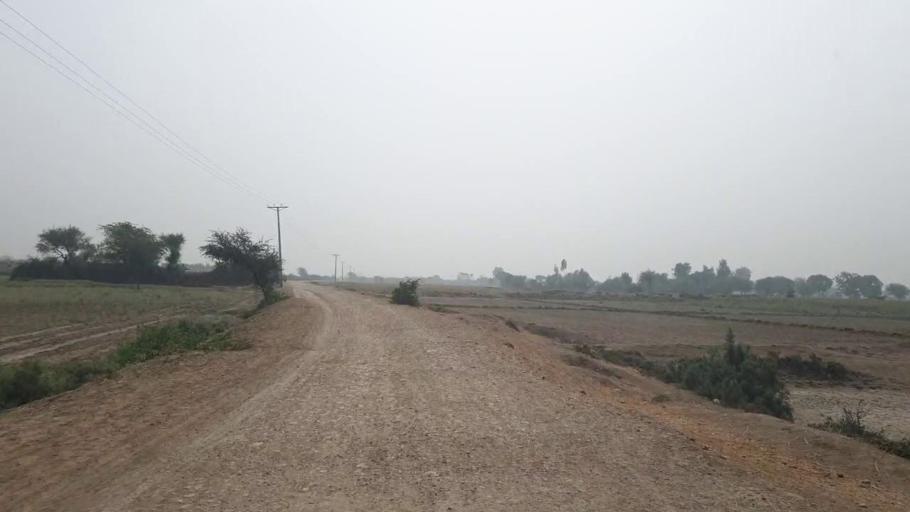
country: PK
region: Sindh
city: Kario
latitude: 24.6417
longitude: 68.6403
